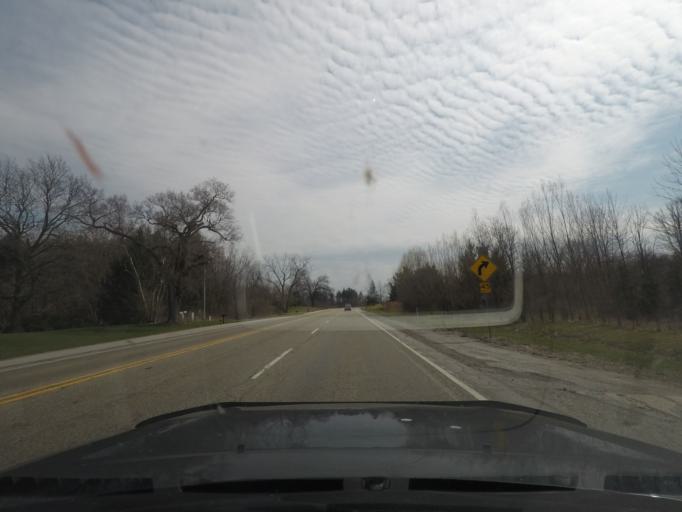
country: US
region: Indiana
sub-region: LaPorte County
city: LaPorte
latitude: 41.6595
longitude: -86.7679
